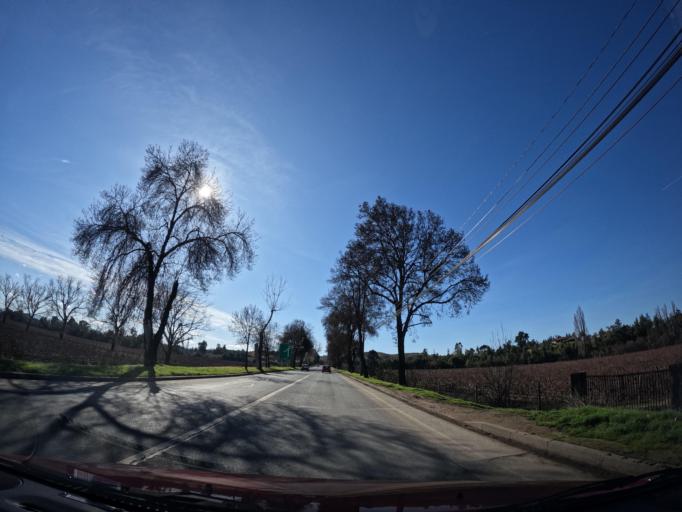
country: CL
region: Maule
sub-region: Provincia de Cauquenes
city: Cauquenes
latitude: -35.9590
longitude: -72.3117
